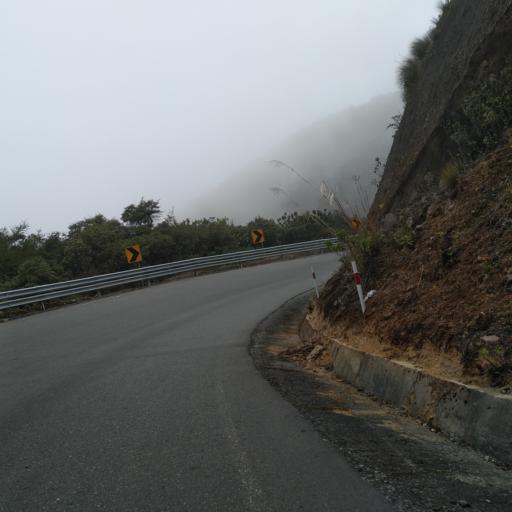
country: EC
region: Cotopaxi
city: La Mana
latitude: -0.9884
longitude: -78.9705
